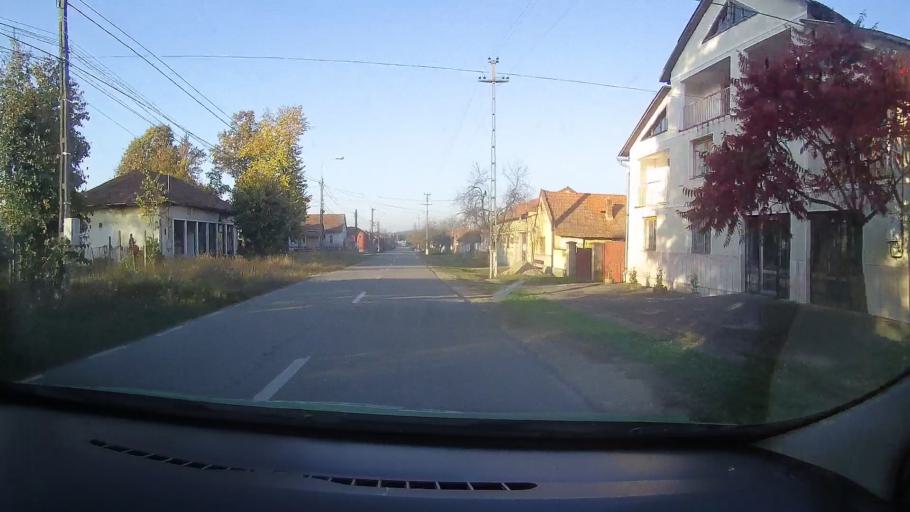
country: RO
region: Timis
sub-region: Comuna Fardea
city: Fardea
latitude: 45.7380
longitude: 22.1637
